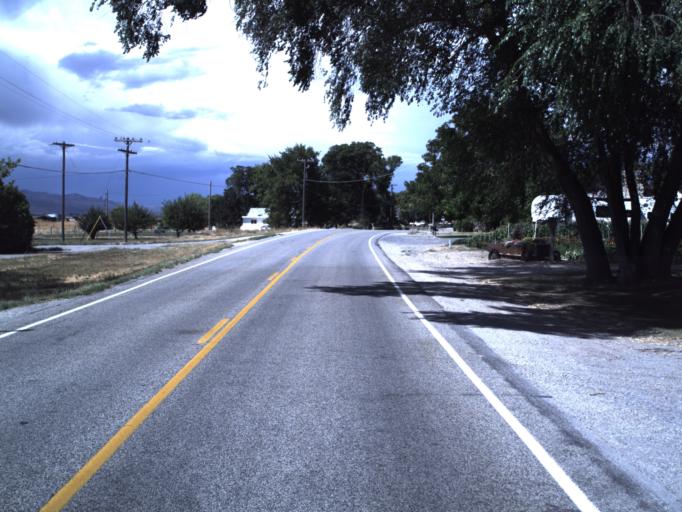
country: US
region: Utah
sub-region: Box Elder County
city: Honeyville
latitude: 41.6694
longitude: -112.0894
